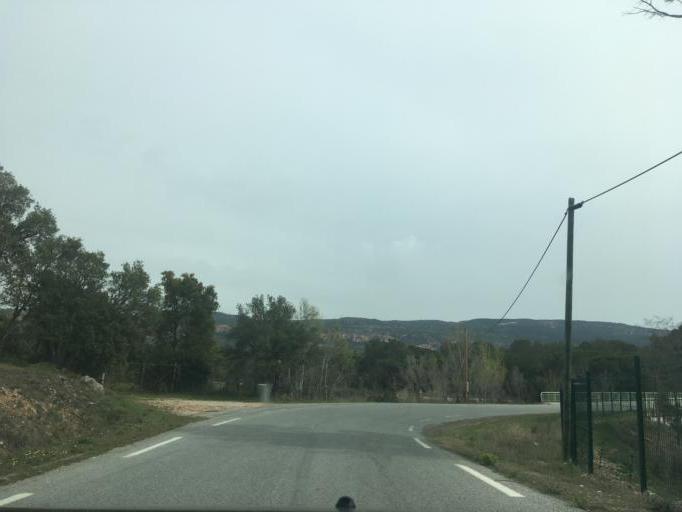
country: FR
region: Provence-Alpes-Cote d'Azur
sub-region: Departement du Var
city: Le Muy
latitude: 43.5029
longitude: 6.5885
